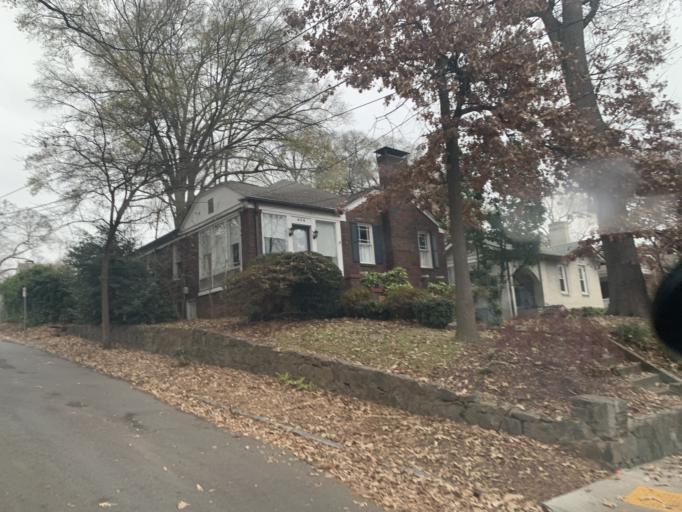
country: US
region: Georgia
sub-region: Fulton County
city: Atlanta
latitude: 33.7795
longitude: -84.3741
